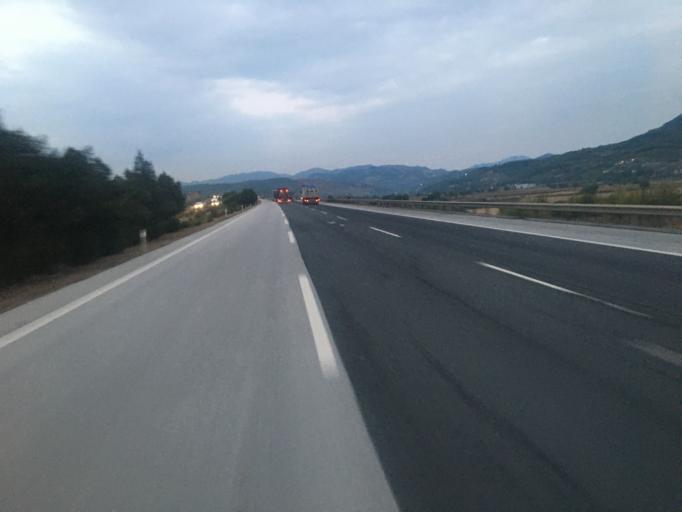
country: TR
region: Osmaniye
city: Osmaniye
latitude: 37.1505
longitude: 36.3438
